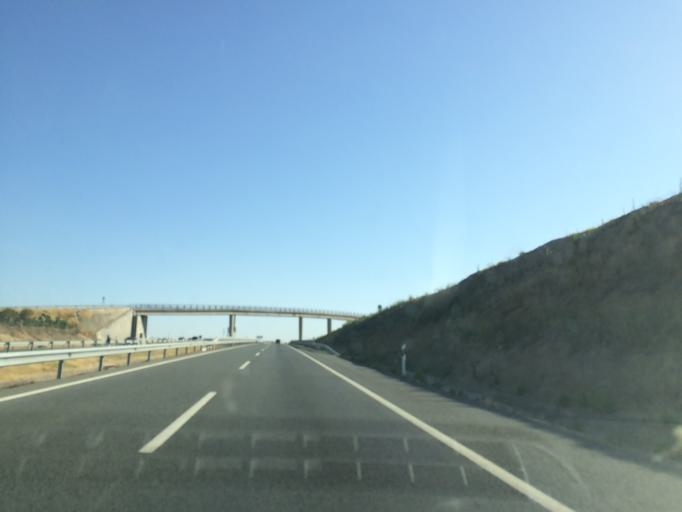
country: ES
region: Castille-La Mancha
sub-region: Province of Toledo
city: Maqueda
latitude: 40.0660
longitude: -4.3665
